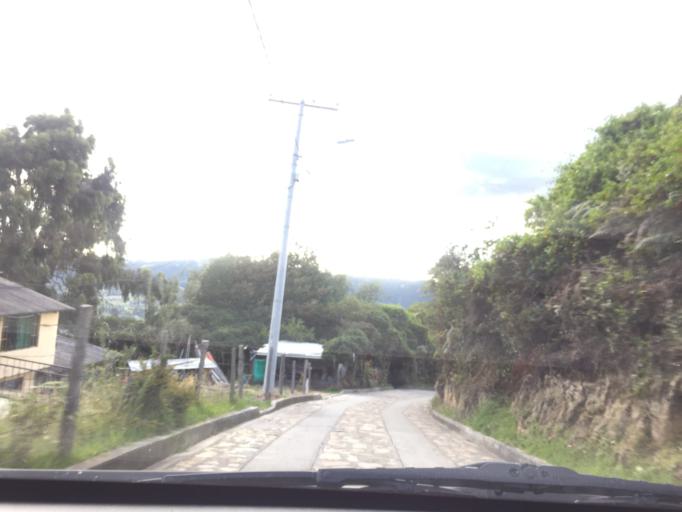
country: CO
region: Cundinamarca
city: Sopo
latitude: 4.9135
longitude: -73.9269
